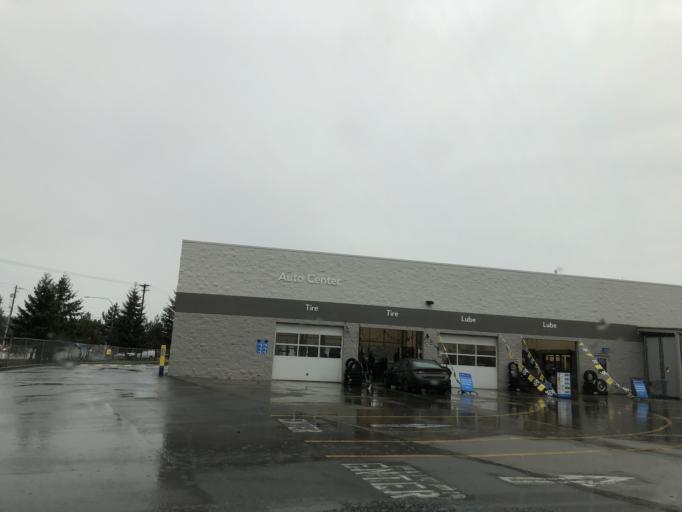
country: US
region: Washington
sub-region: Pierce County
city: Elk Plain
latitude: 47.0732
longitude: -122.4204
